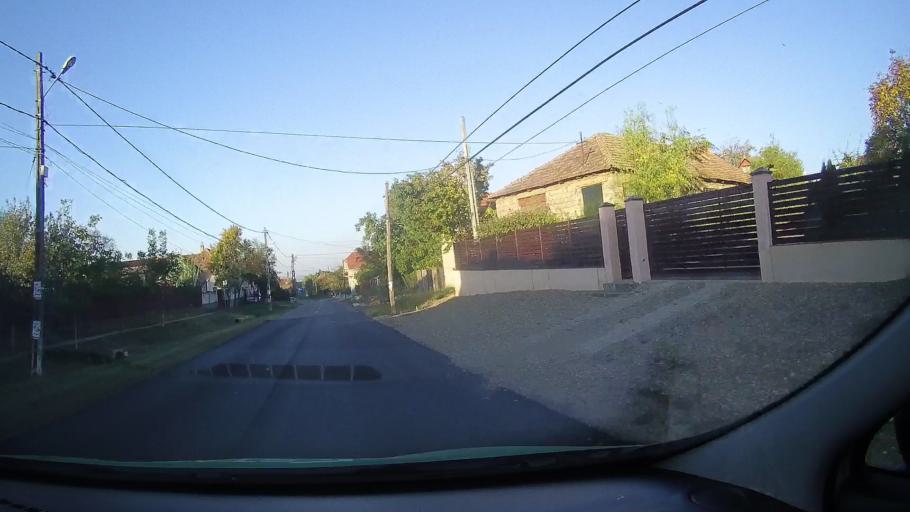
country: RO
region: Bihor
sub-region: Comuna Cetariu
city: Cetariu
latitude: 47.1444
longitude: 21.9994
